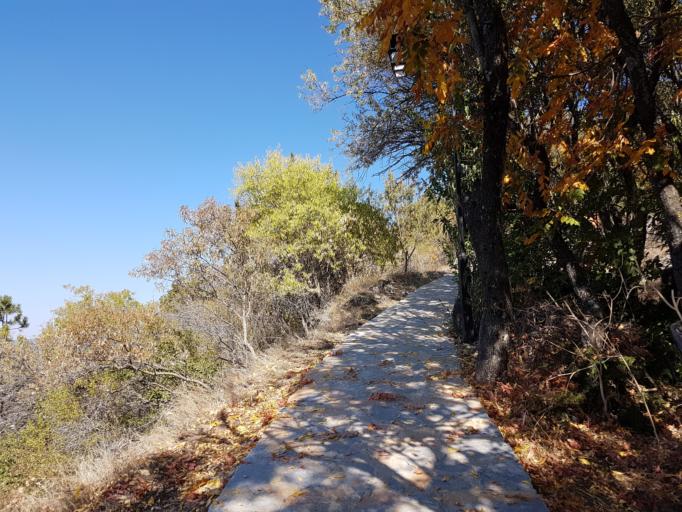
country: MK
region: Ohrid
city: Ohrid
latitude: 41.1149
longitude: 20.7881
